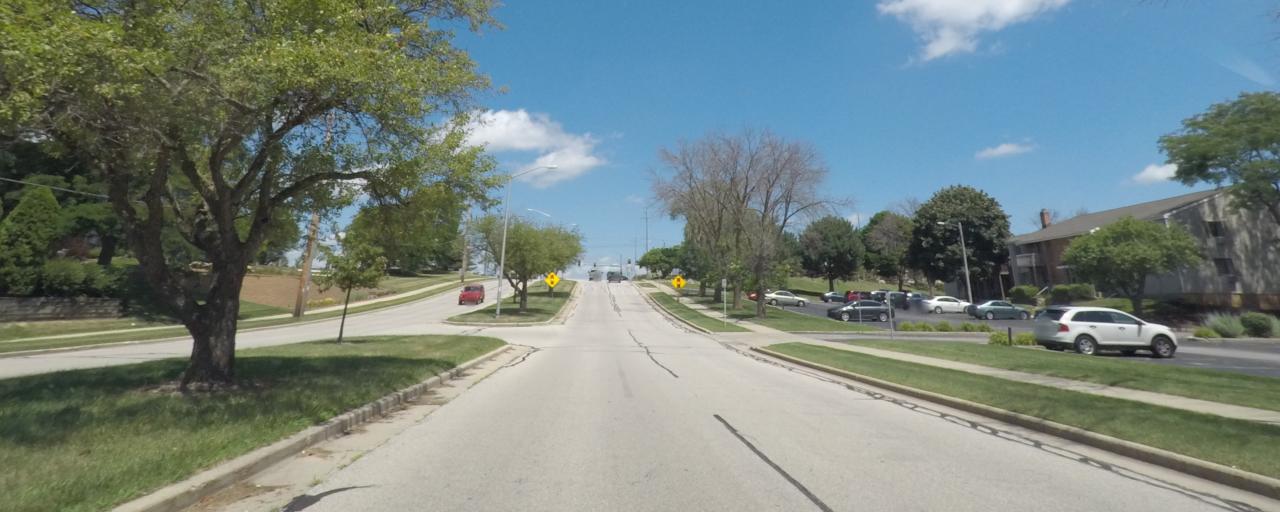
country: US
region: Wisconsin
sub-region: Waukesha County
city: Waukesha
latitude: 43.0348
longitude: -88.1859
